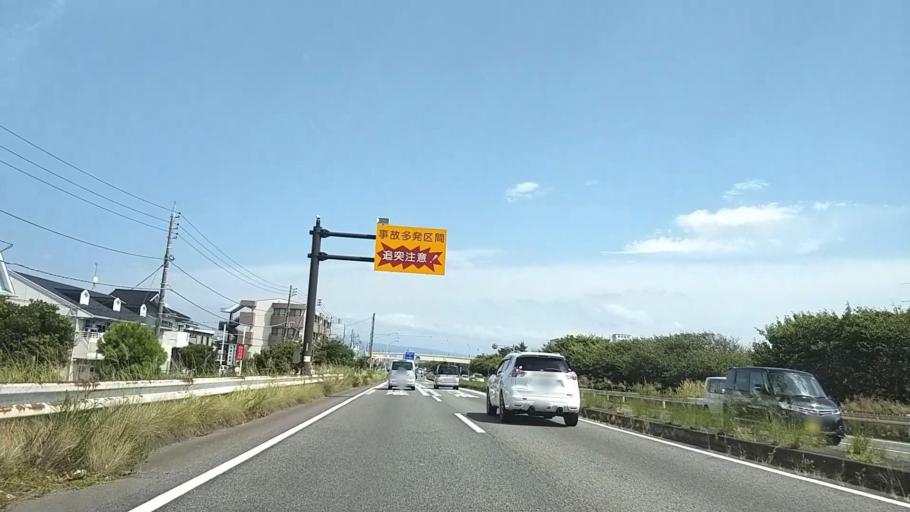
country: JP
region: Shizuoka
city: Numazu
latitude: 35.1287
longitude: 138.7978
